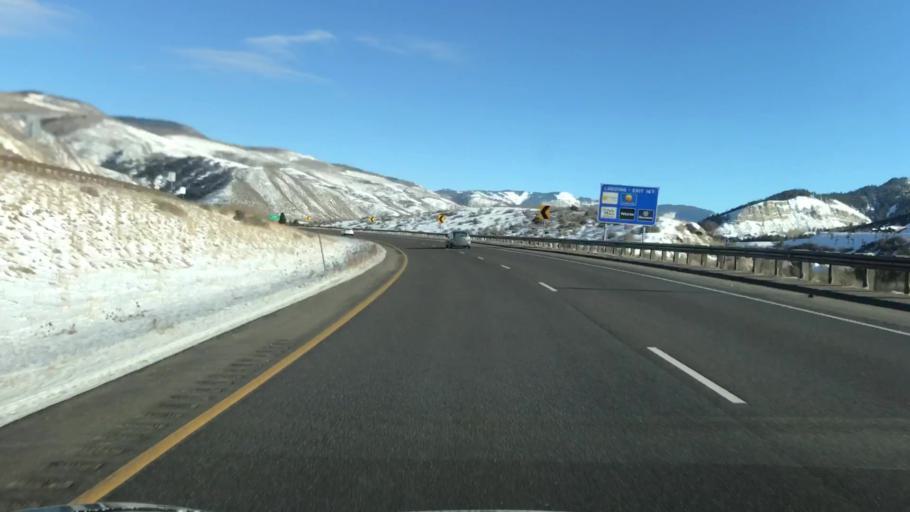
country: US
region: Colorado
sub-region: Eagle County
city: Avon
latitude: 39.6378
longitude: -106.5457
